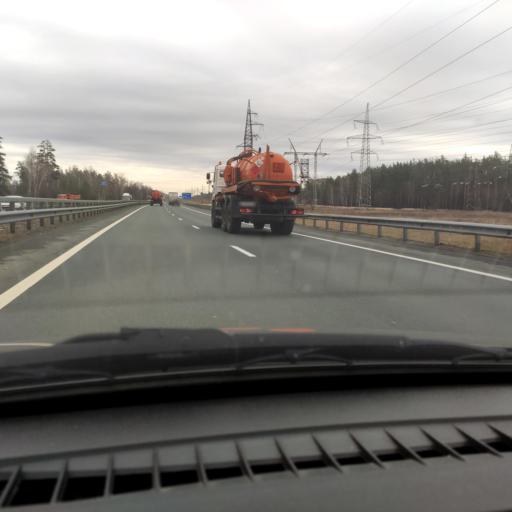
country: RU
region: Samara
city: Pribrezhnyy
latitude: 53.5184
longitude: 49.8187
